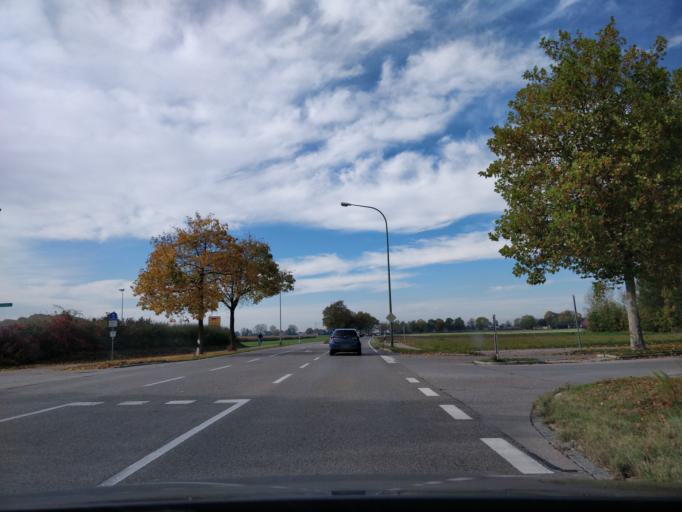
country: DE
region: Bavaria
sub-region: Swabia
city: Konigsbrunn
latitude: 48.2508
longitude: 10.8925
